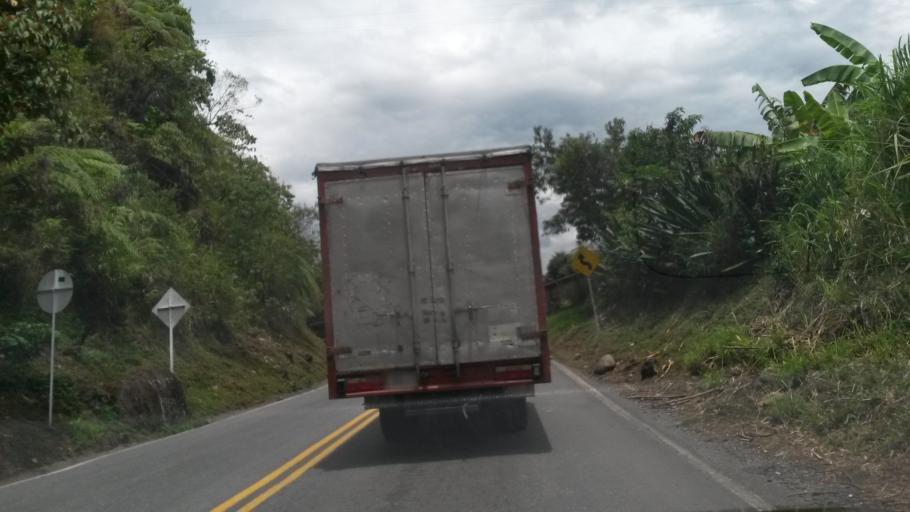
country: CO
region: Cauca
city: Rosas
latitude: 2.2606
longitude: -76.7518
